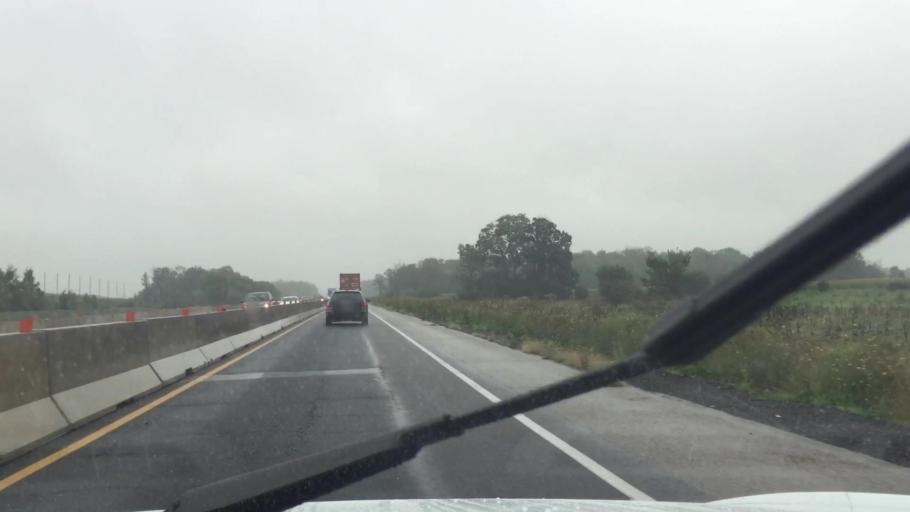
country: CA
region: Ontario
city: Delaware
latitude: 42.8064
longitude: -81.3301
